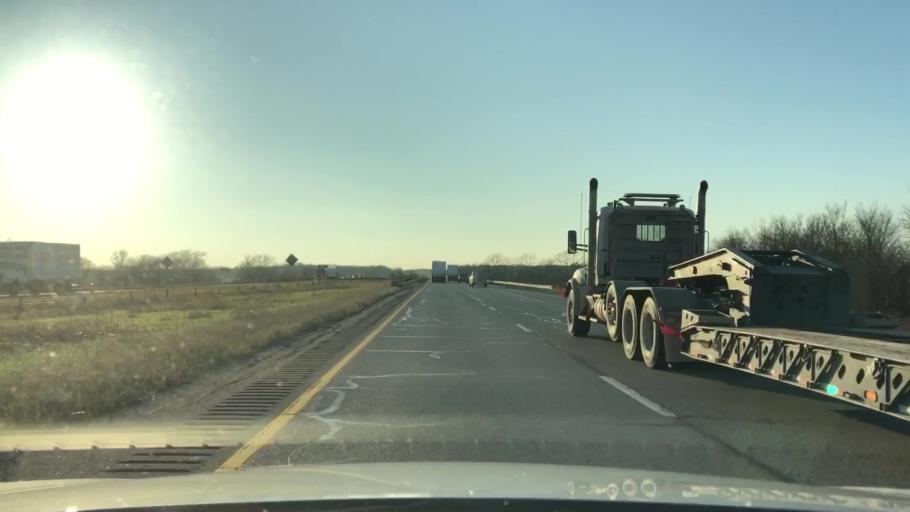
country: US
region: Texas
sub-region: Caldwell County
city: Luling
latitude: 29.6520
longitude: -97.5992
